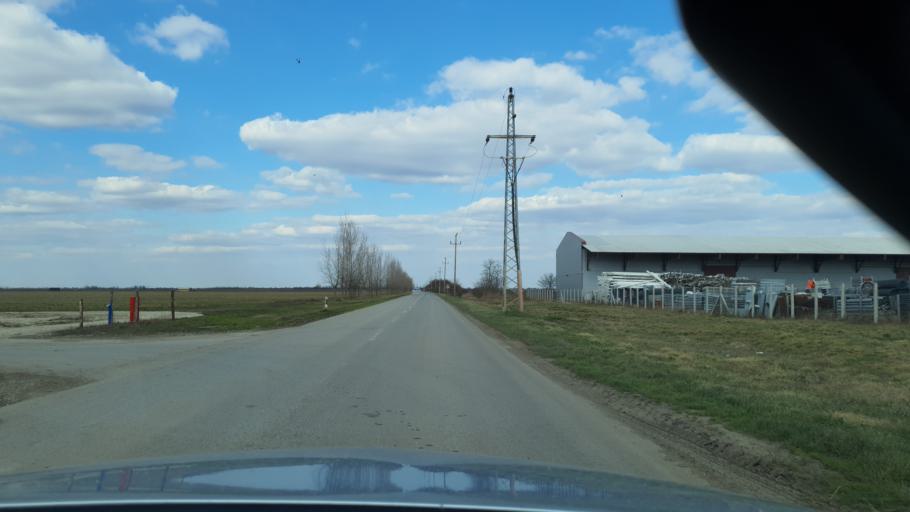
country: RS
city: Kulpin
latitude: 45.4213
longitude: 19.5993
